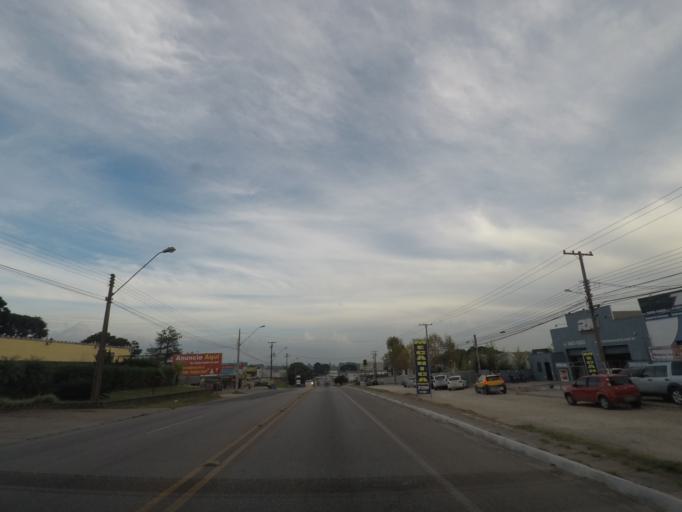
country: BR
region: Parana
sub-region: Colombo
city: Colombo
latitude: -25.3568
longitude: -49.2193
